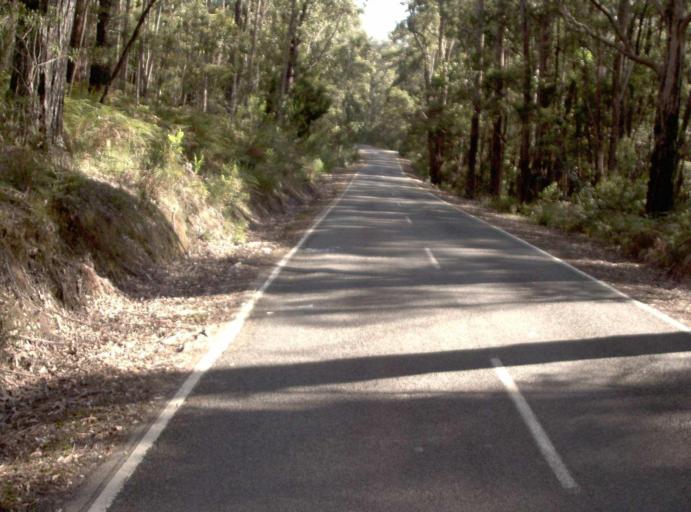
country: AU
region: Victoria
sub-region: East Gippsland
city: Lakes Entrance
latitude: -37.6219
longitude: 148.5111
